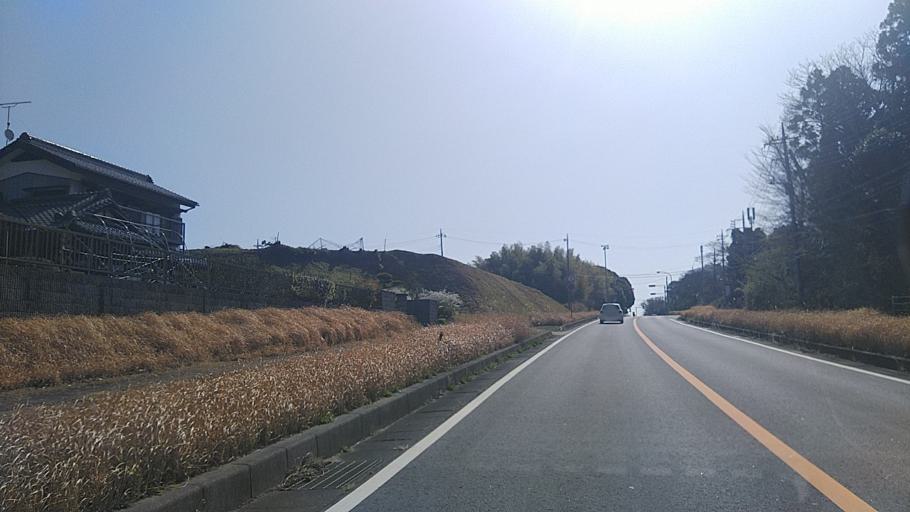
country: JP
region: Ibaraki
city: Fujishiro
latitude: 35.8839
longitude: 140.1171
